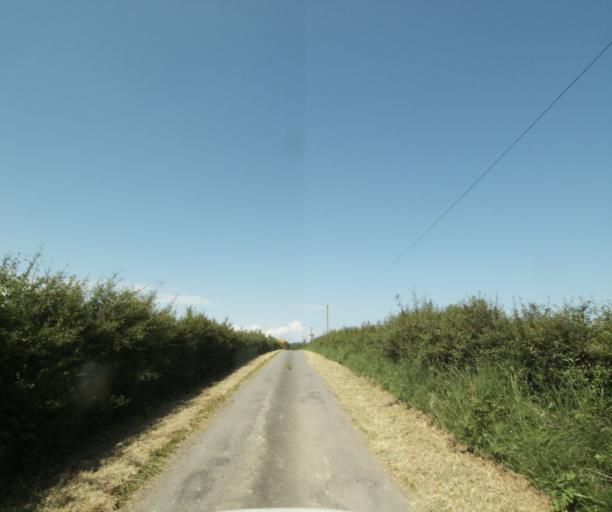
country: FR
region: Bourgogne
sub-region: Departement de Saone-et-Loire
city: Palinges
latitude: 46.5666
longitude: 4.1930
